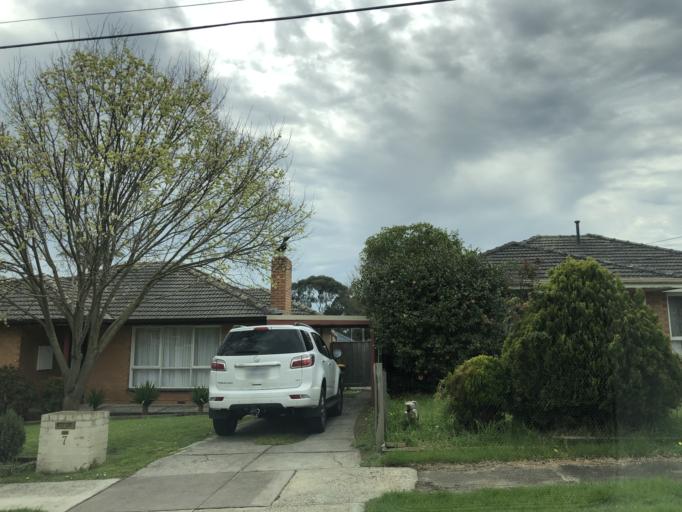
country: AU
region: Victoria
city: Burwood East
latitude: -37.8485
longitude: 145.1386
